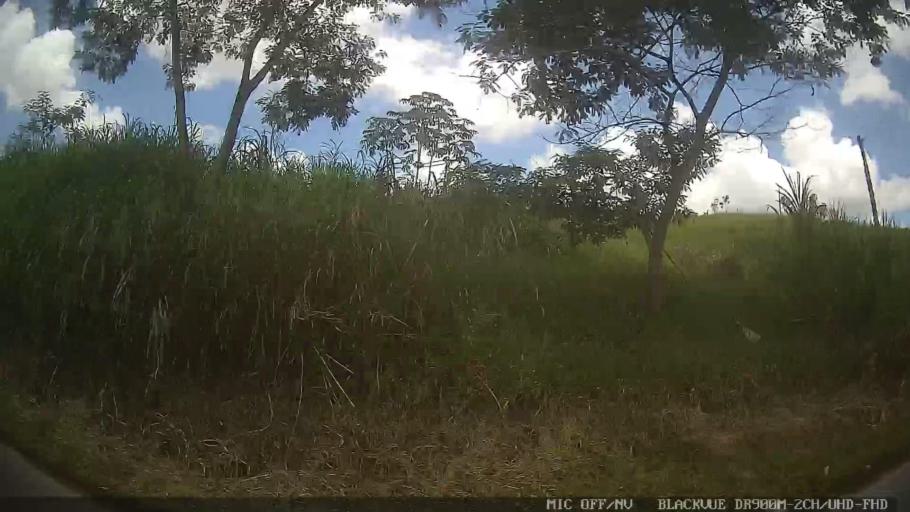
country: BR
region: Sao Paulo
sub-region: Jacarei
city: Jacarei
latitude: -23.3111
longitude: -45.9312
